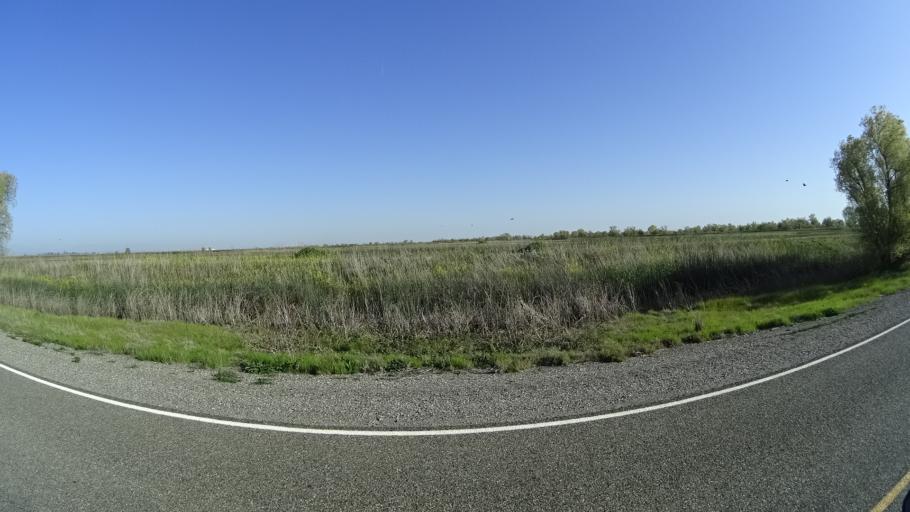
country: US
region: California
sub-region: Glenn County
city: Willows
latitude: 39.4074
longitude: -122.1469
